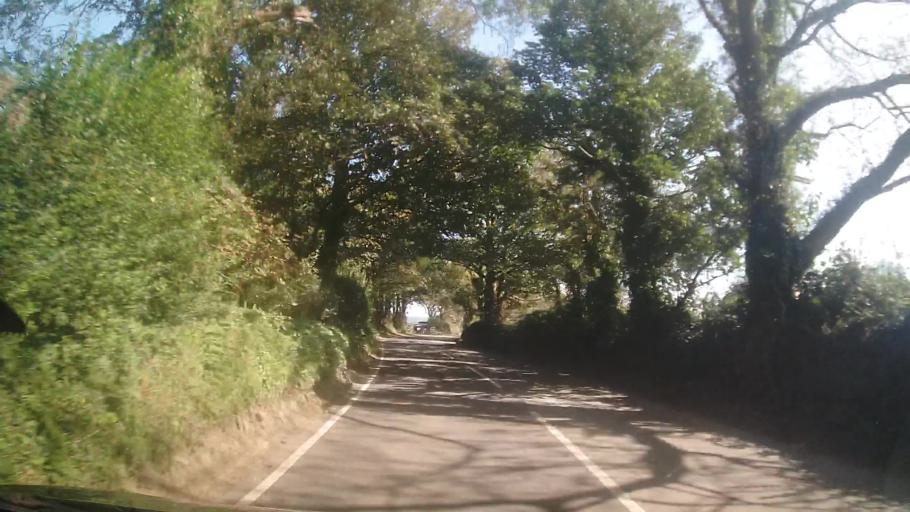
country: GB
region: Wales
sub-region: Pembrokeshire
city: Mathry
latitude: 51.9429
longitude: -5.0518
